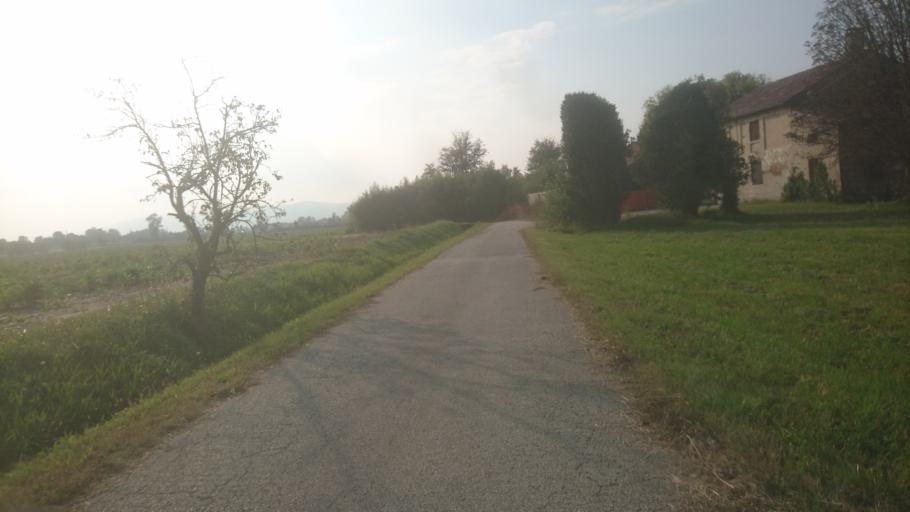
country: IT
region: Veneto
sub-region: Provincia di Vicenza
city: Grumolo delle Abbadesse
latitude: 45.5016
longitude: 11.6650
